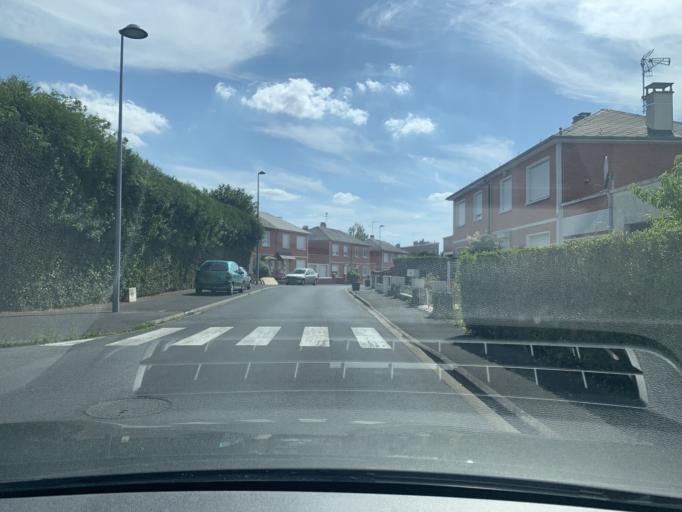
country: FR
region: Nord-Pas-de-Calais
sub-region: Departement du Nord
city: Cambrai
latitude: 50.1588
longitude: 3.2580
